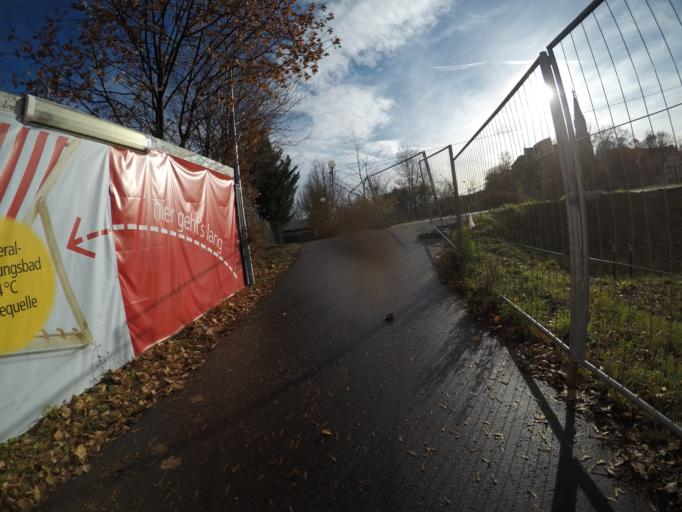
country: DE
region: Baden-Wuerttemberg
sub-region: Regierungsbezirk Stuttgart
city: Stuttgart-Ost
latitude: 48.7979
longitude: 9.2106
